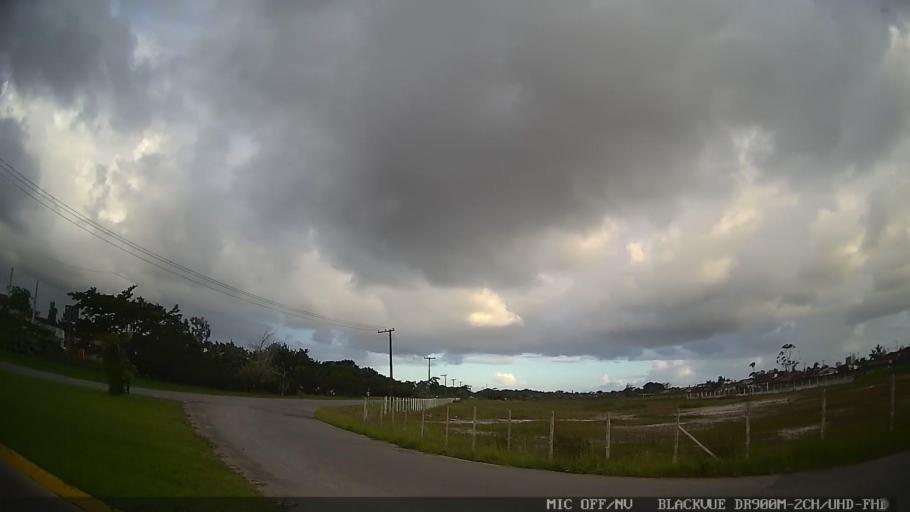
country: BR
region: Sao Paulo
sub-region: Itanhaem
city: Itanhaem
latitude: -24.1646
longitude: -46.7832
